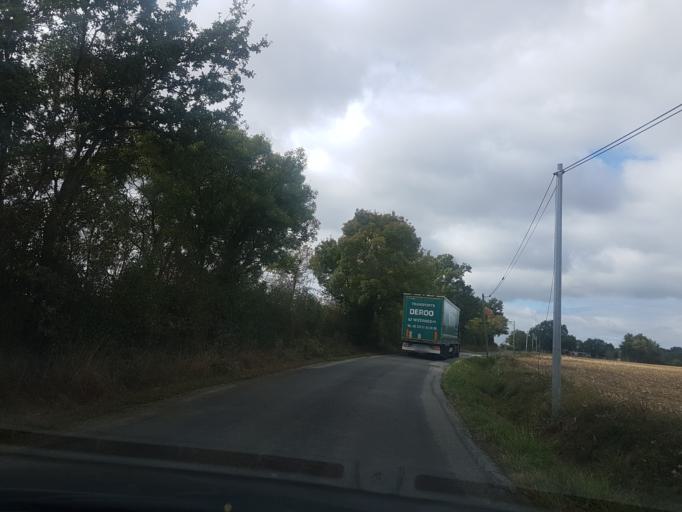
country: FR
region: Pays de la Loire
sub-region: Departement de la Loire-Atlantique
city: Ligne
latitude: 47.3984
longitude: -1.3974
